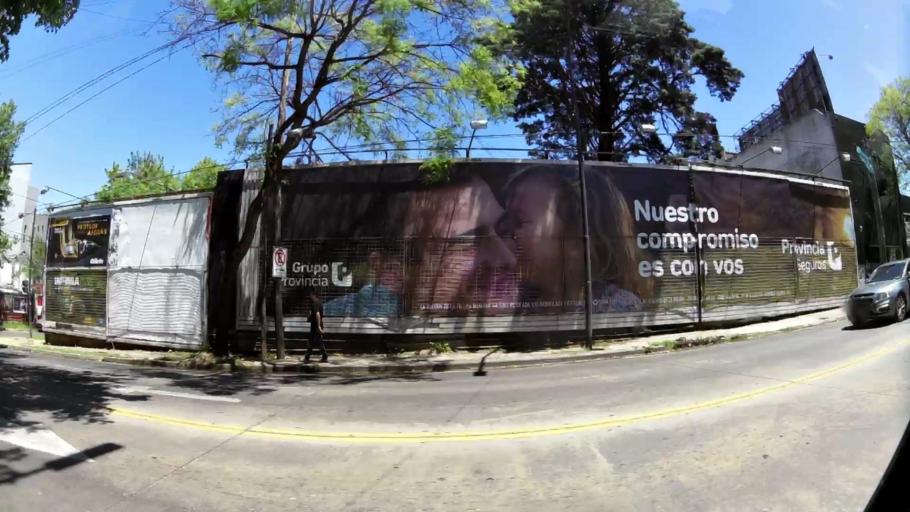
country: AR
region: Buenos Aires
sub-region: Partido de Vicente Lopez
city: Olivos
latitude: -34.4994
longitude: -58.4838
